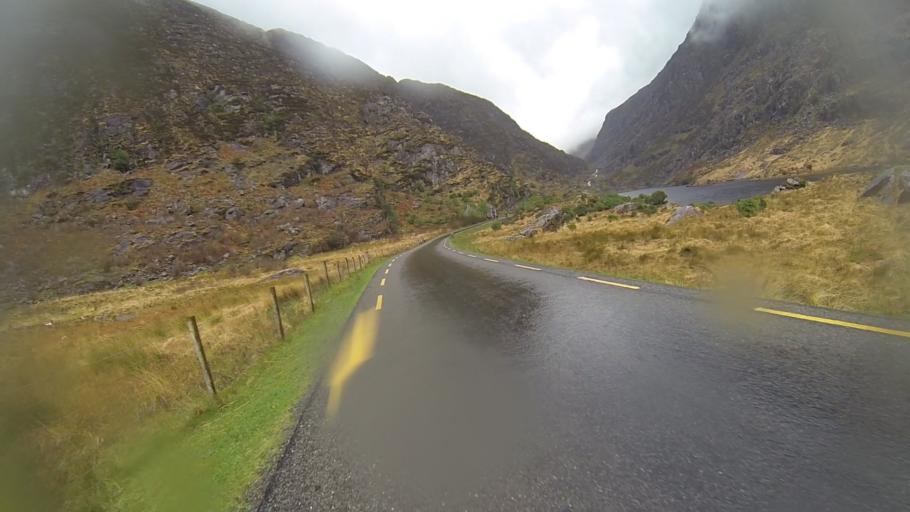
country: IE
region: Munster
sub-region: Ciarrai
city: Cill Airne
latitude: 52.0150
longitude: -9.6353
